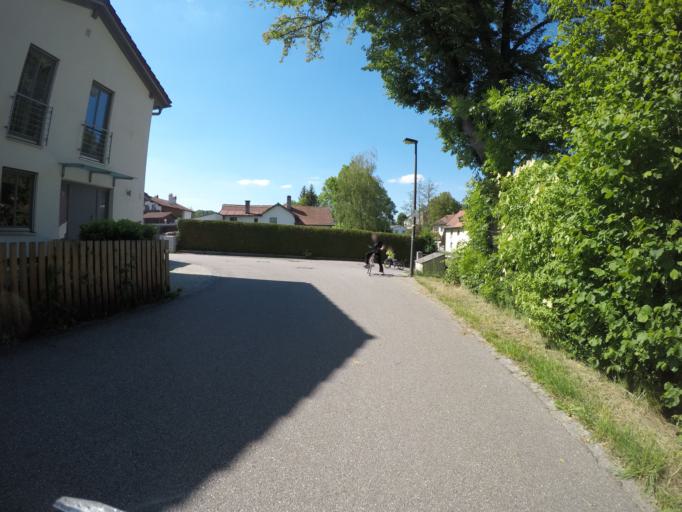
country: DE
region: Bavaria
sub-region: Lower Bavaria
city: Landshut
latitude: 48.5199
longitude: 12.1486
